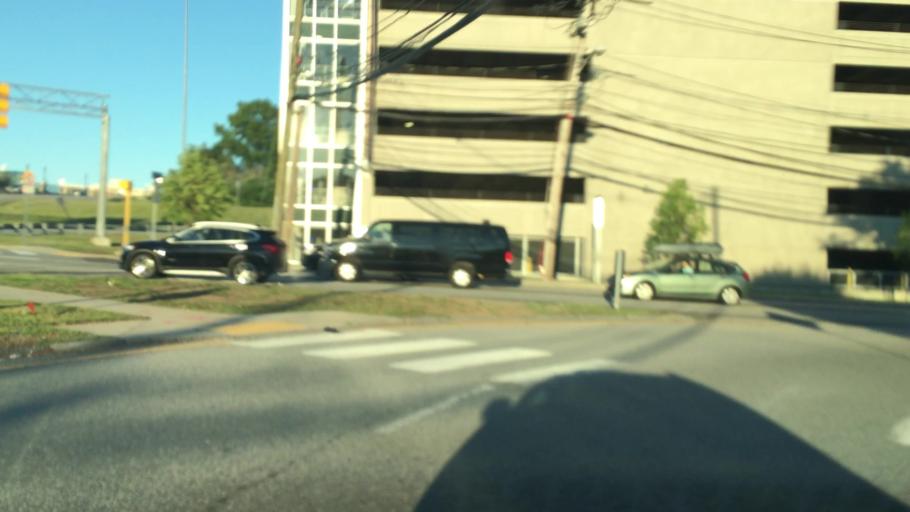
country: US
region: Massachusetts
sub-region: Middlesex County
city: Waltham
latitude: 42.3971
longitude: -71.2641
